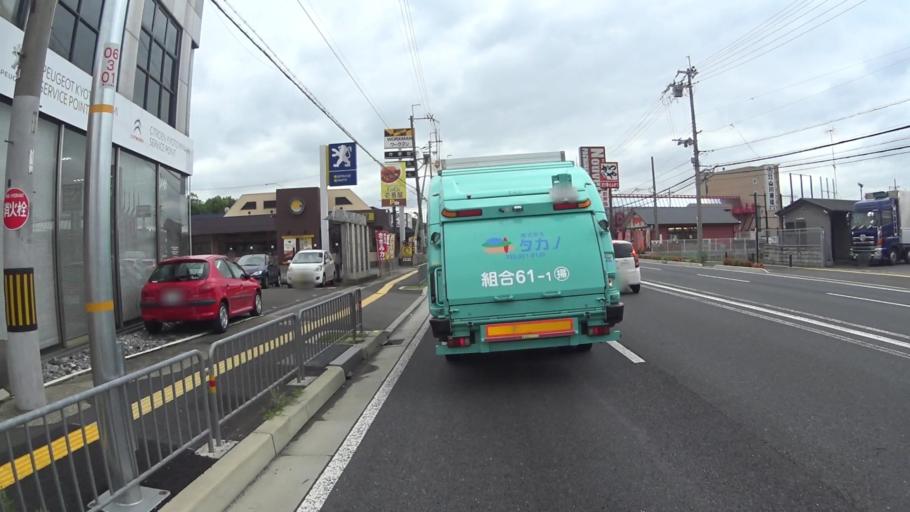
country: JP
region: Kyoto
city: Muko
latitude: 34.9399
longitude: 135.7163
